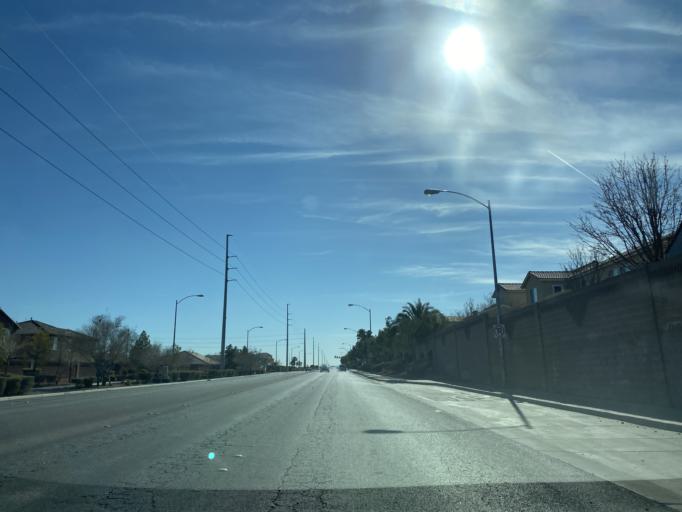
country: US
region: Nevada
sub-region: Clark County
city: North Las Vegas
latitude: 36.2317
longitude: -115.1435
